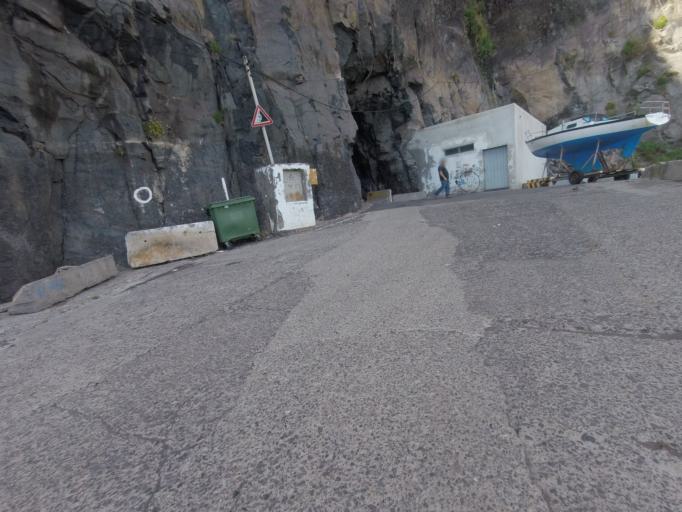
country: PT
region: Madeira
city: Ribeira Brava
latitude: 32.6689
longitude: -17.0641
